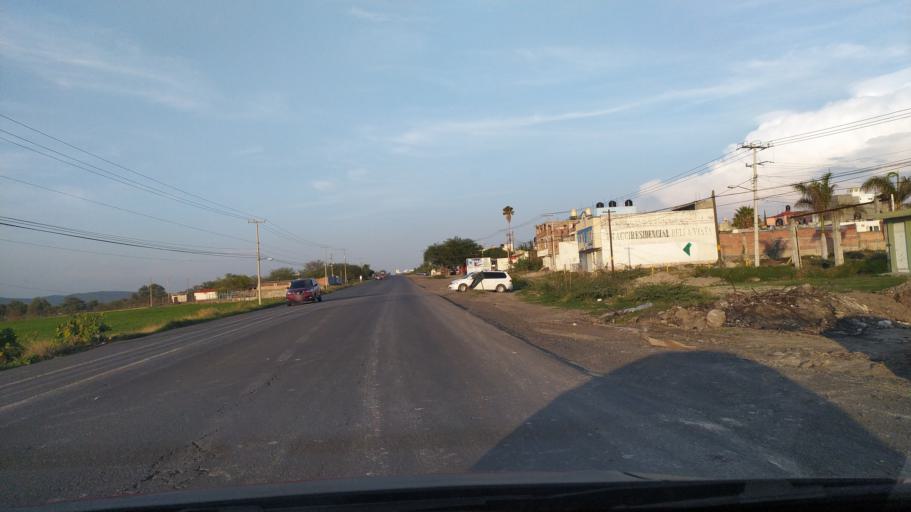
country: MX
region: Michoacan
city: Vistahermosa de Negrete
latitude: 20.2662
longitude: -102.4692
